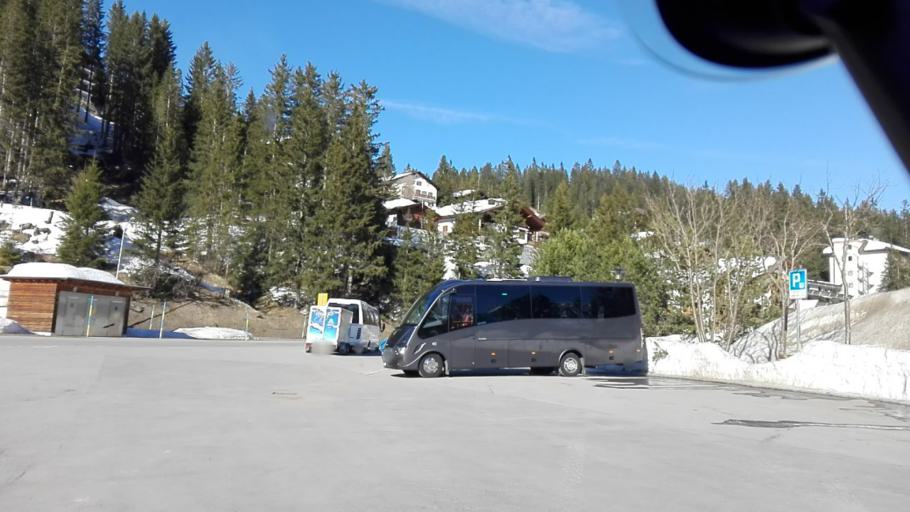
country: CH
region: Grisons
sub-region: Plessur District
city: Arosa
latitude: 46.7860
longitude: 9.6802
